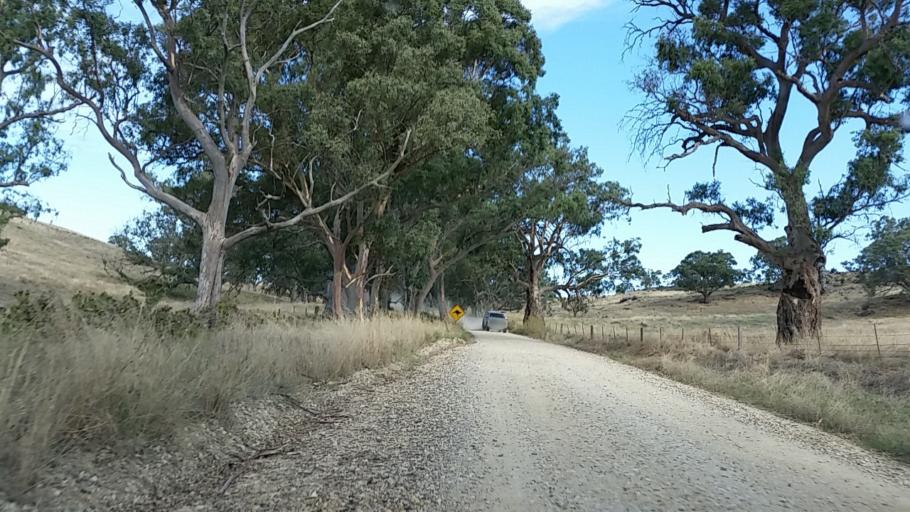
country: AU
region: South Australia
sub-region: Barossa
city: Angaston
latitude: -34.5603
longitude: 139.0976
